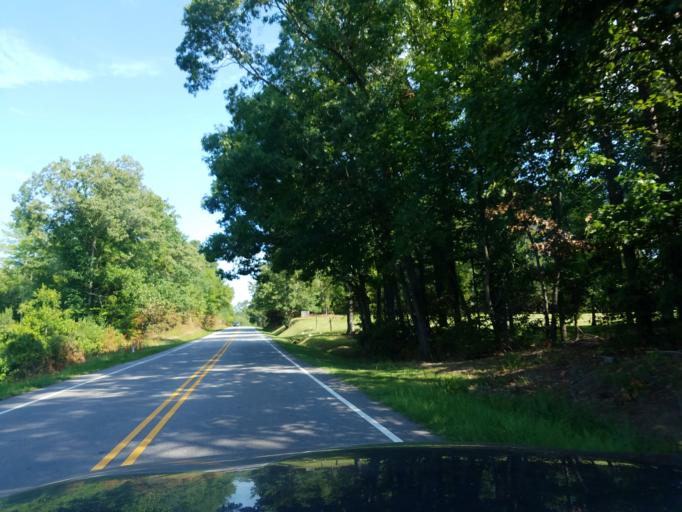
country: US
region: North Carolina
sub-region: Vance County
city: Henderson
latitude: 36.3497
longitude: -78.4165
